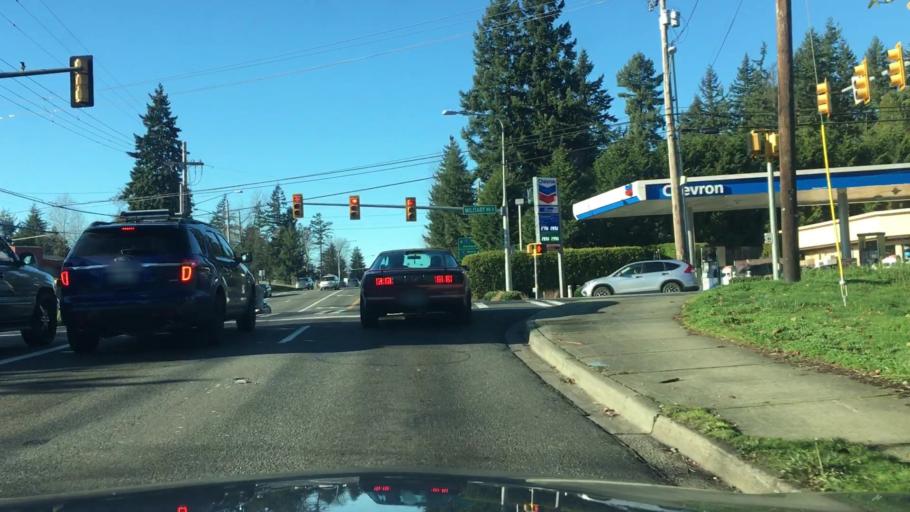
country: US
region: Washington
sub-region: King County
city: Lakeland North
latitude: 47.3579
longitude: -122.2917
